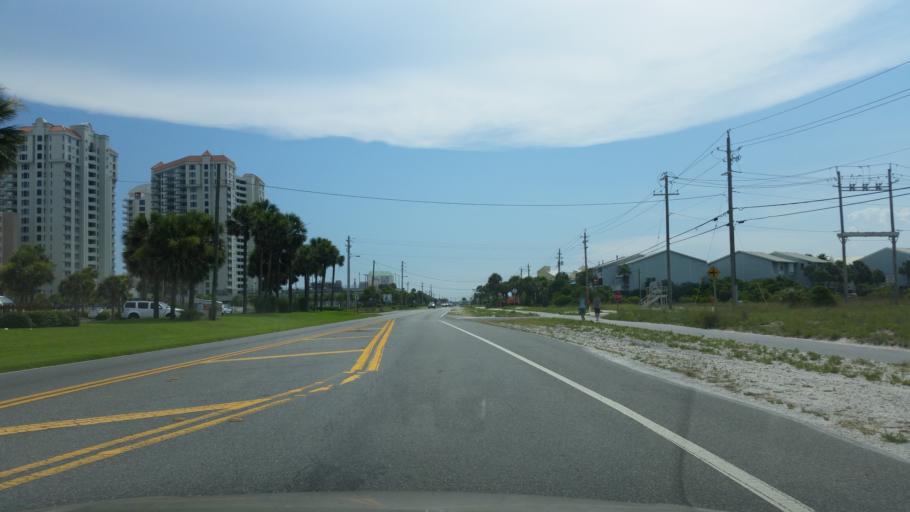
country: US
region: Florida
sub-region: Santa Rosa County
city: Navarre
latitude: 30.3813
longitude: -86.8646
